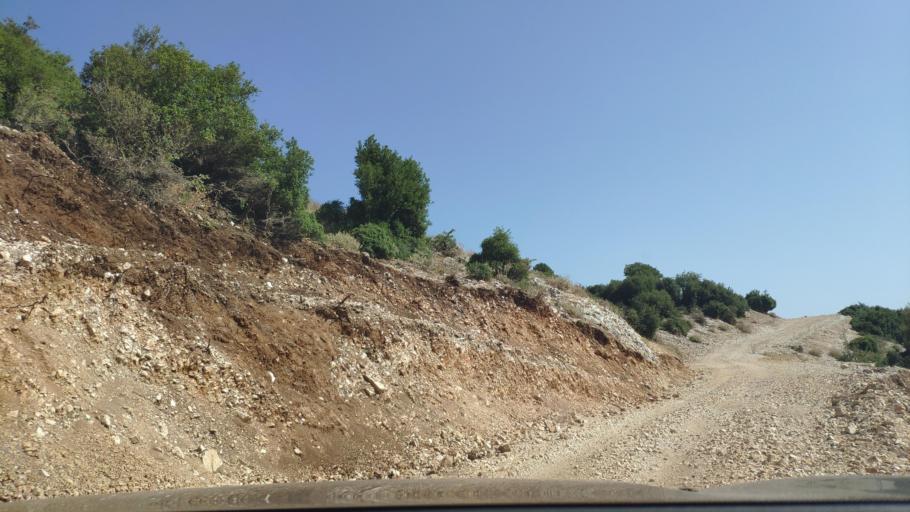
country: GR
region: West Greece
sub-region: Nomos Aitolias kai Akarnanias
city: Monastirakion
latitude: 38.8051
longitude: 20.9975
